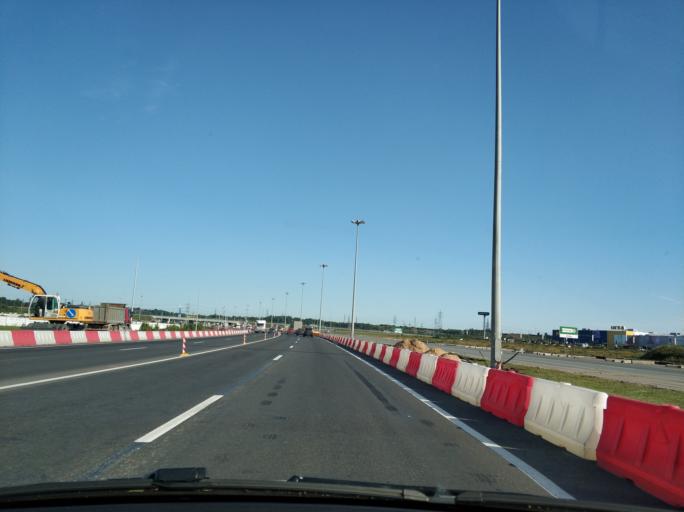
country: RU
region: Leningrad
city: Bugry
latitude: 60.0865
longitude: 30.3764
